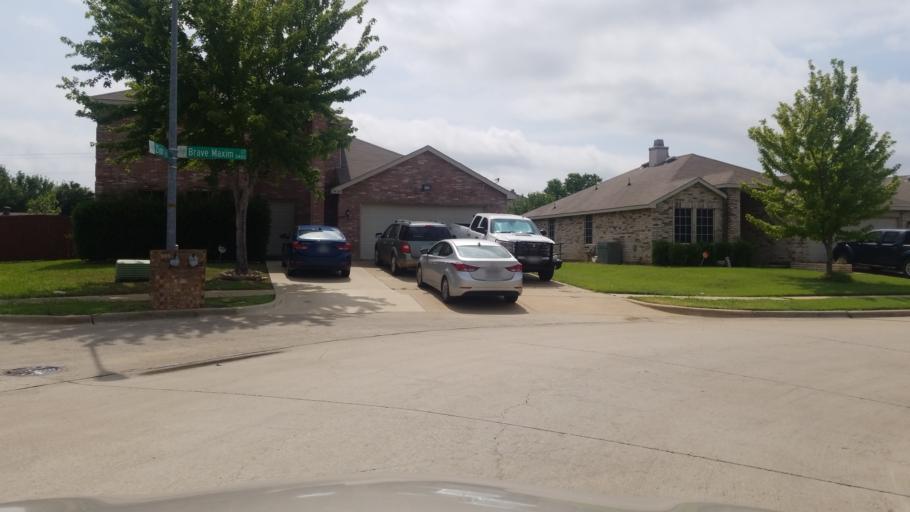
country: US
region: Texas
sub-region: Dallas County
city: Grand Prairie
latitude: 32.6891
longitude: -97.0317
